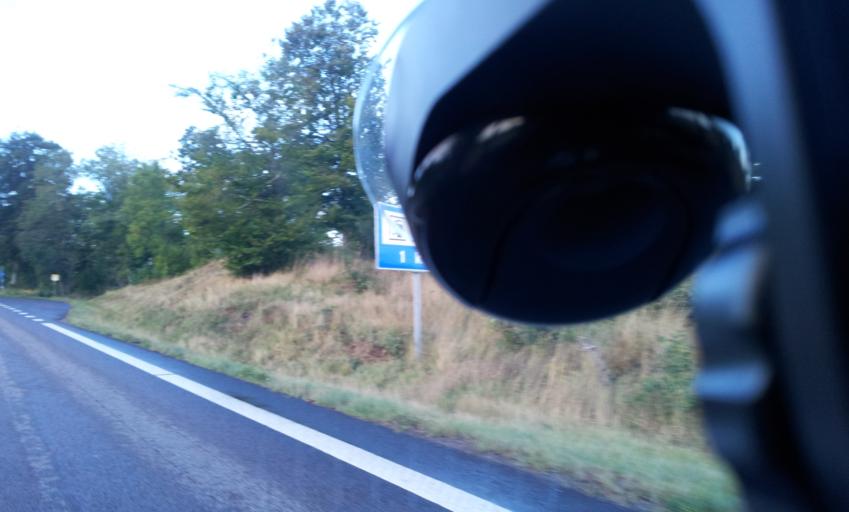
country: SE
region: Kalmar
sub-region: Monsteras Kommun
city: Moensteras
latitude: 57.0608
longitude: 16.4463
